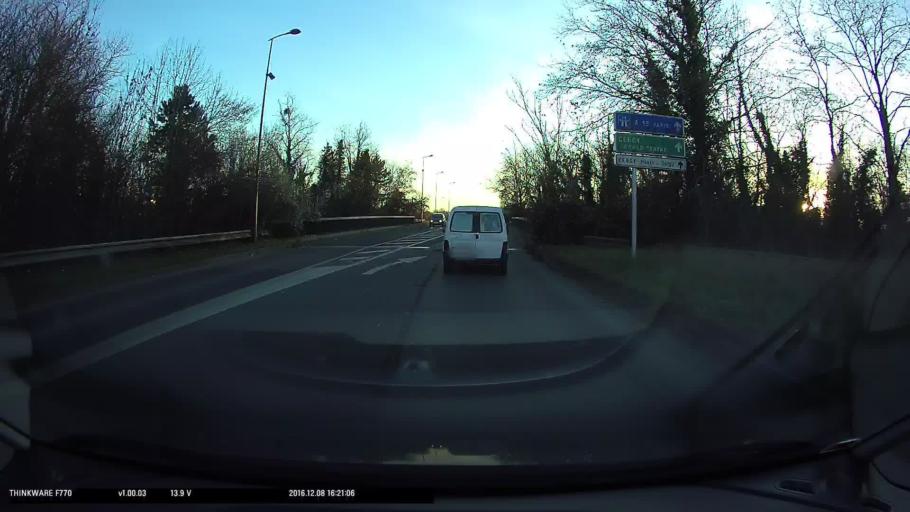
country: FR
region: Ile-de-France
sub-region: Departement du Val-d'Oise
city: Vaureal
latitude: 49.0593
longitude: 2.0308
